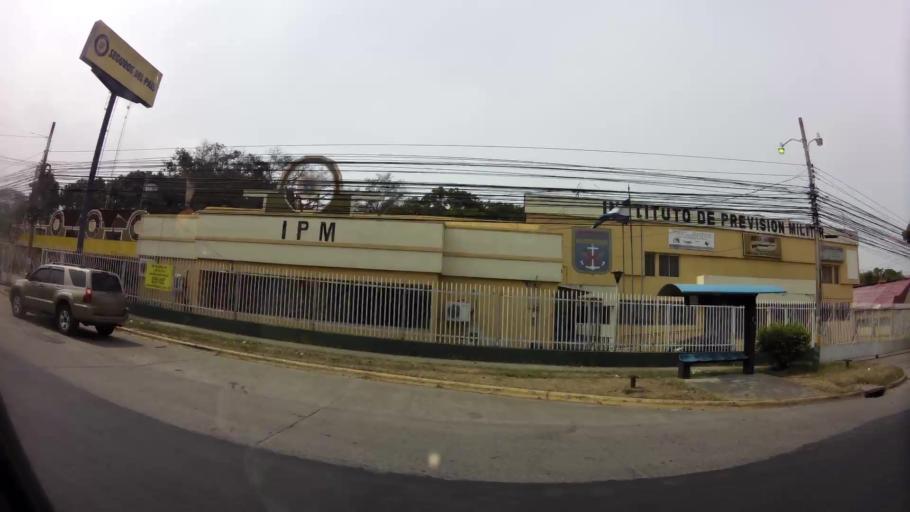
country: HN
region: Cortes
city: San Pedro Sula
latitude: 15.5185
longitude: -88.0274
